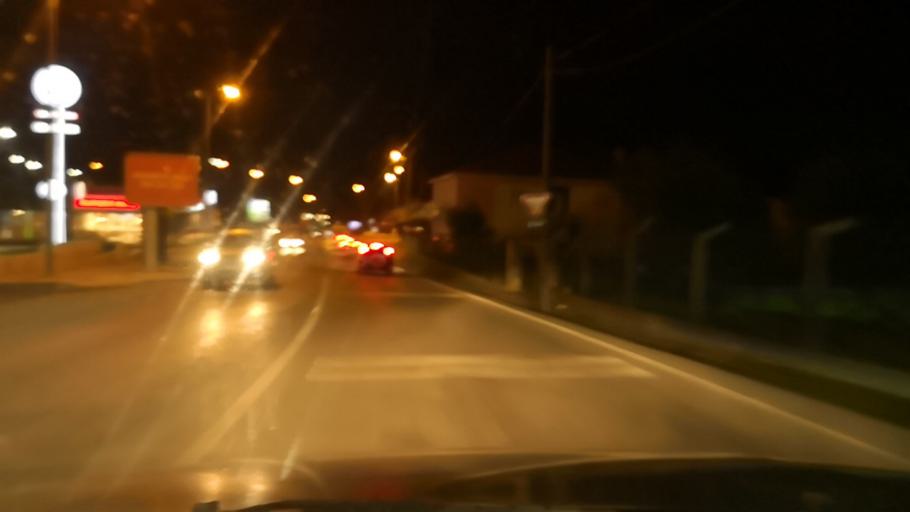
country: PT
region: Setubal
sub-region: Palmela
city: Palmela
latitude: 38.5770
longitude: -8.8965
